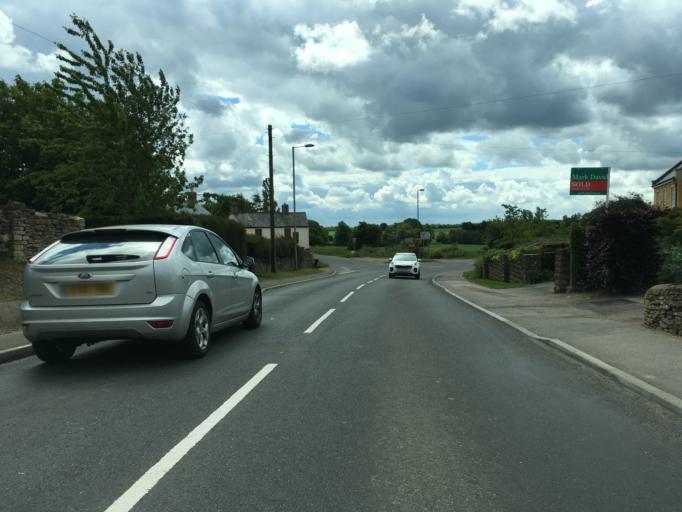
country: GB
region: England
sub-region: Oxfordshire
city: Chipping Norton
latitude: 51.9350
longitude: -1.5415
